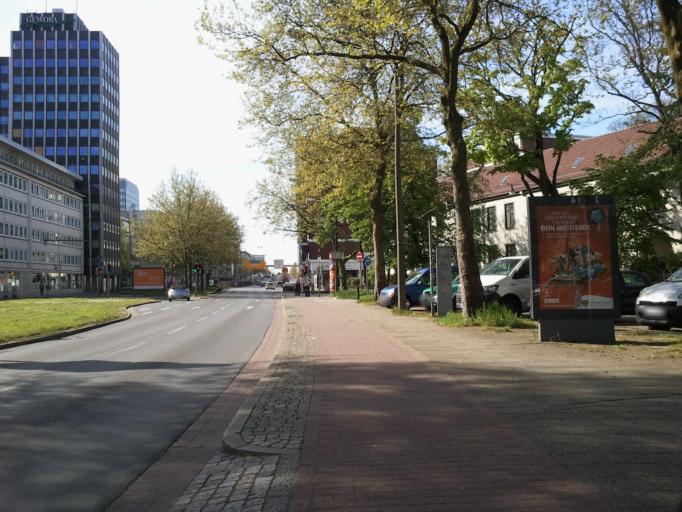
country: DE
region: Bremen
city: Bremen
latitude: 53.0783
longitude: 8.8180
